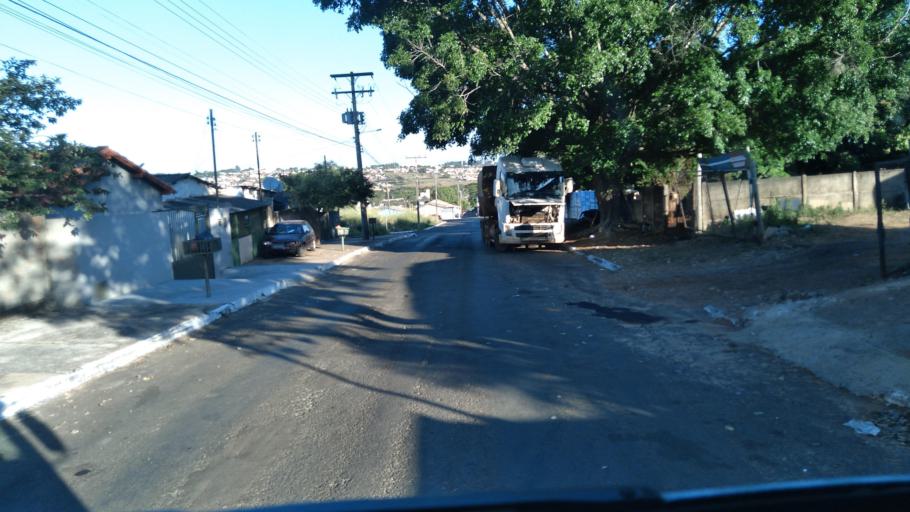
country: BR
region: Goias
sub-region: Mineiros
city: Mineiros
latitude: -17.5589
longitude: -52.5471
